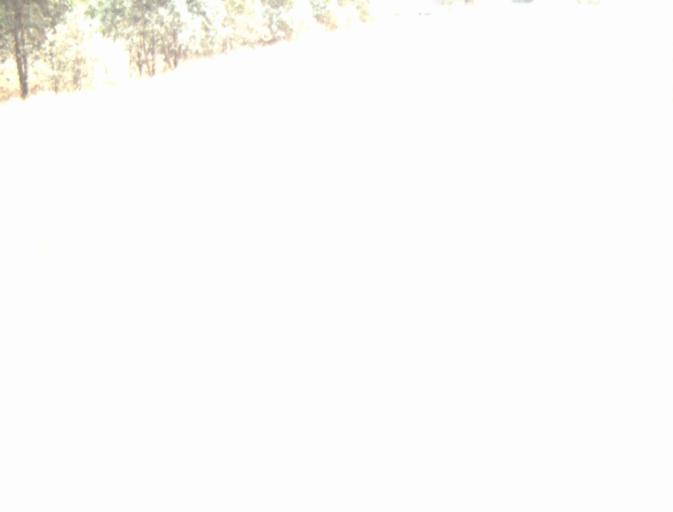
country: AU
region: Tasmania
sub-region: Northern Midlands
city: Evandale
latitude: -41.4779
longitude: 147.5145
